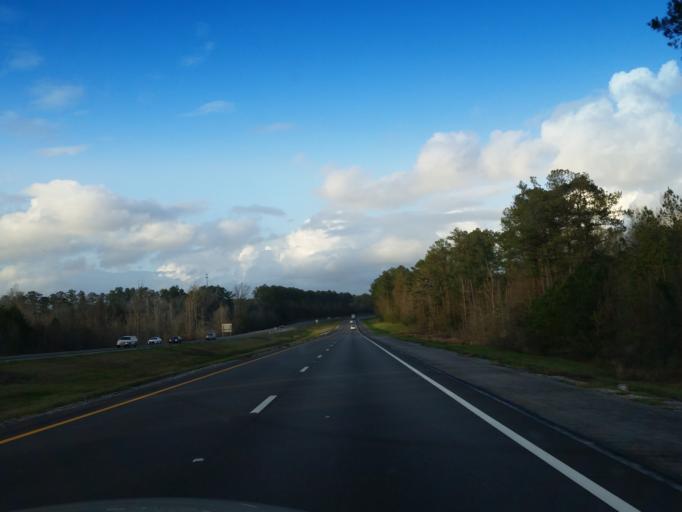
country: US
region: Mississippi
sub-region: Jones County
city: Sharon
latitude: 31.8670
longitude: -89.0461
